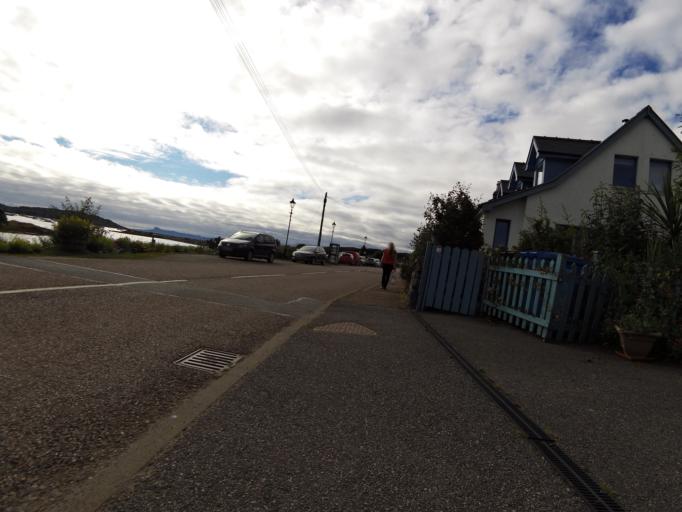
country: GB
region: Scotland
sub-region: Argyll and Bute
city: Isle Of Mull
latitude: 56.9094
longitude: -5.8458
